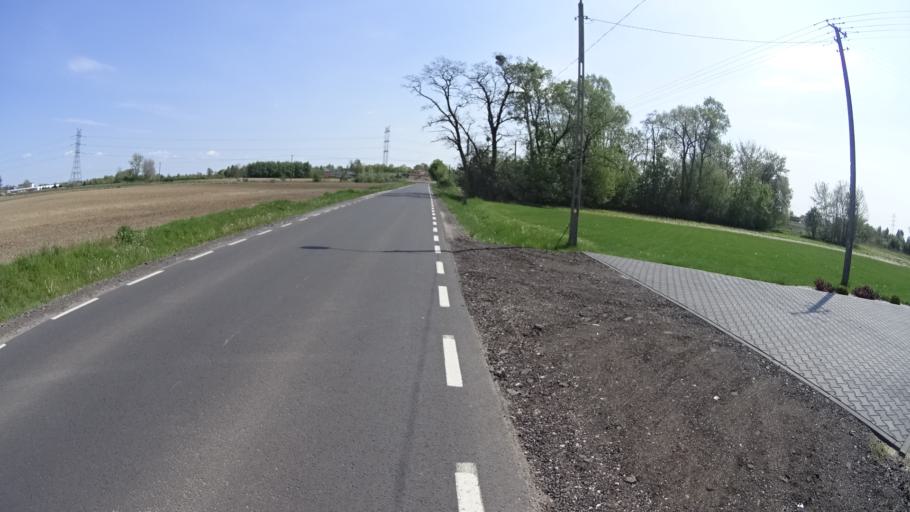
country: PL
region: Masovian Voivodeship
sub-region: Powiat warszawski zachodni
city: Ozarow Mazowiecki
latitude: 52.2354
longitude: 20.7577
